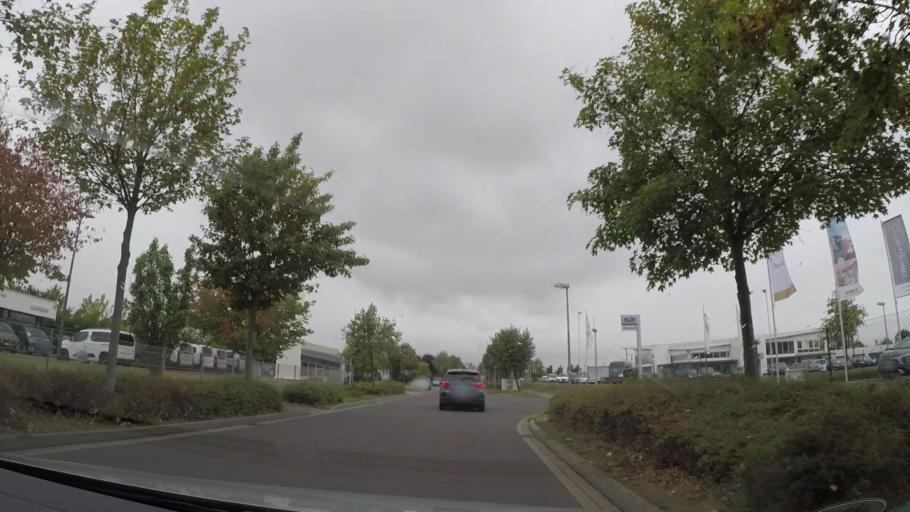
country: DE
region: Saxony-Anhalt
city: Neue Neustadt
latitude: 52.1648
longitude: 11.6053
